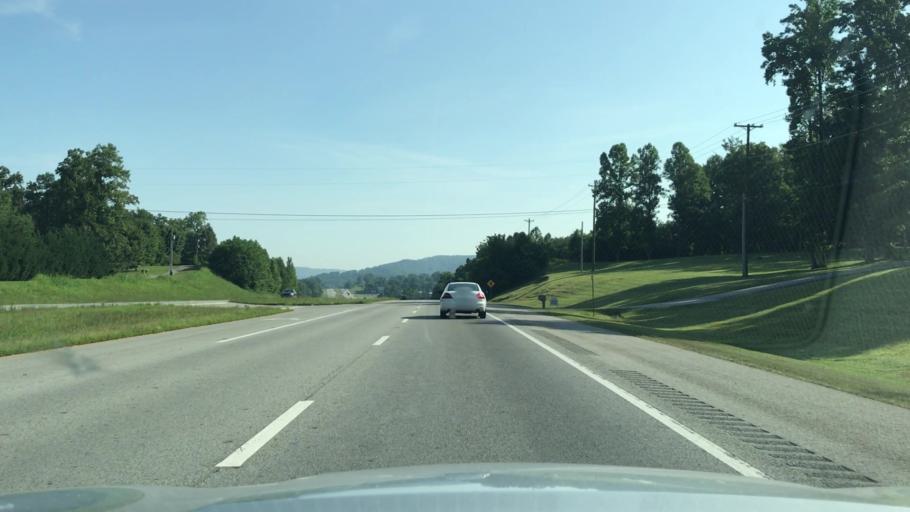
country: US
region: Tennessee
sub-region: Overton County
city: Livingston
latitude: 36.3409
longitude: -85.3486
